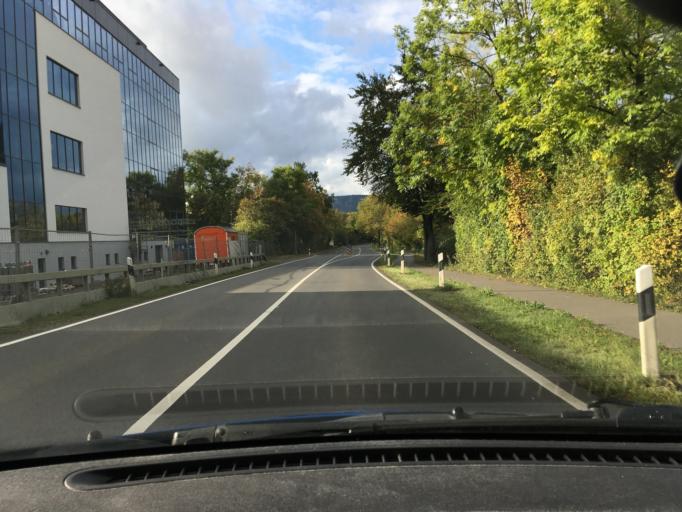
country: DE
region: Lower Saxony
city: Springe
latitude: 52.1935
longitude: 9.5625
